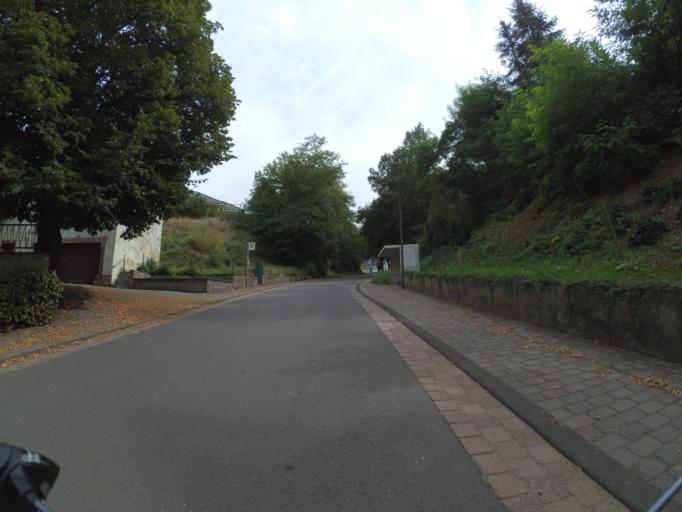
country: DE
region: Rheinland-Pfalz
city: Gladbach
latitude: 49.9348
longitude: 6.7725
